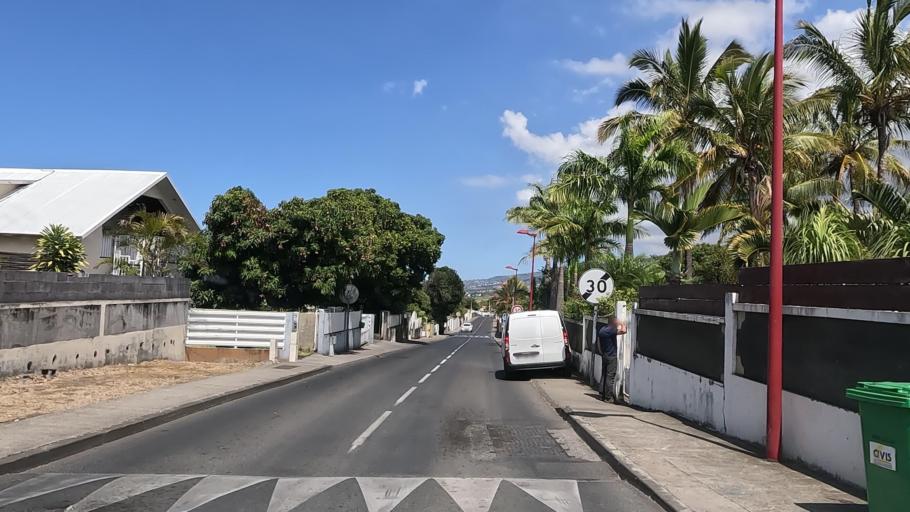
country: RE
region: Reunion
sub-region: Reunion
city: Saint-Louis
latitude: -21.2775
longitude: 55.4463
